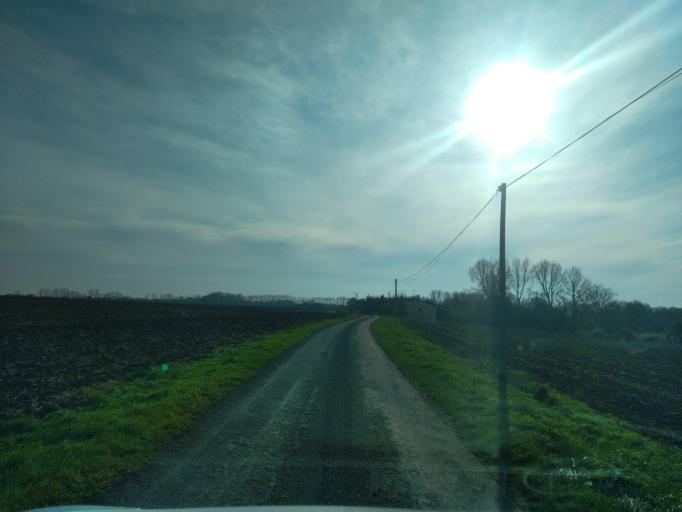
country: FR
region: Pays de la Loire
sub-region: Departement de la Vendee
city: Maillezais
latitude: 46.3542
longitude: -0.7359
